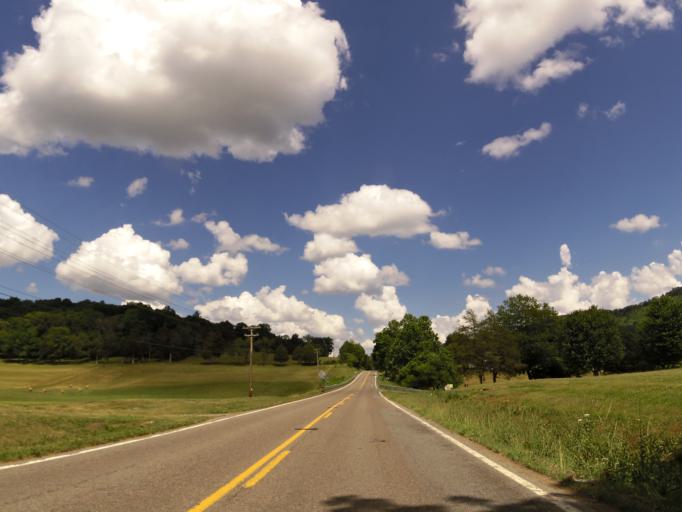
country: US
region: Virginia
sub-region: Lee County
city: Pennington Gap
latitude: 36.6985
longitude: -83.0127
